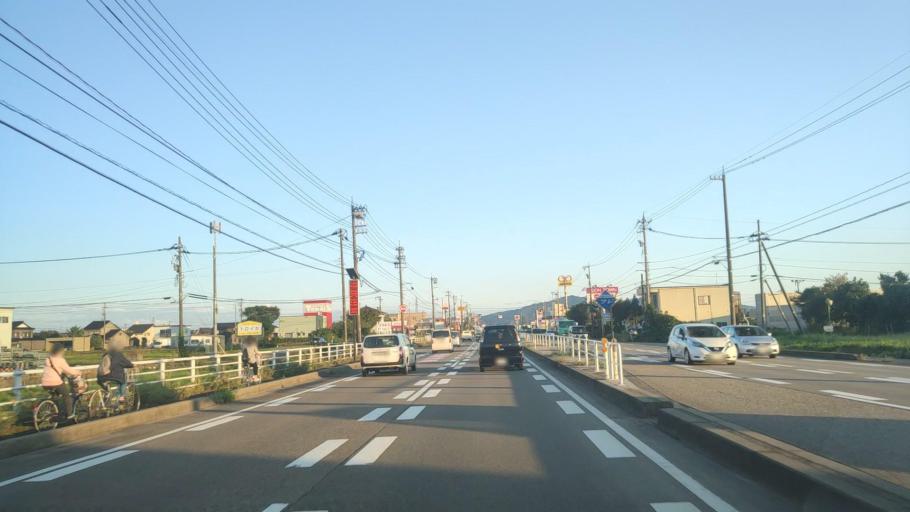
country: JP
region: Toyama
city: Himi
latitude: 36.8414
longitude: 136.9845
